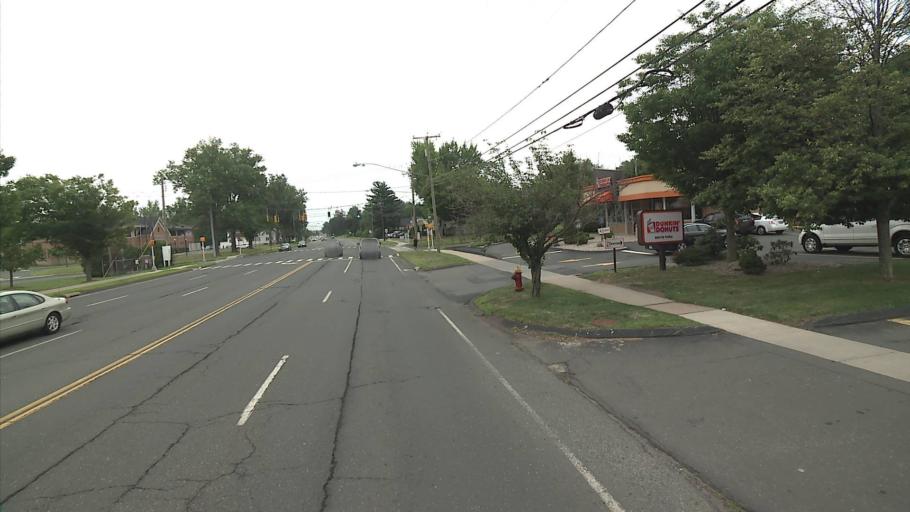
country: US
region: Connecticut
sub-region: Hartford County
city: Wethersfield
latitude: 41.7213
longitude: -72.6677
